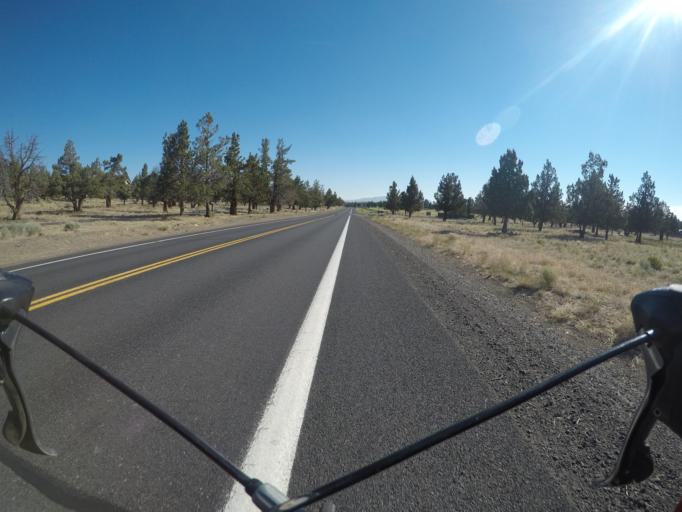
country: US
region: Oregon
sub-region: Deschutes County
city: Redmond
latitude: 44.2579
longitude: -121.2680
